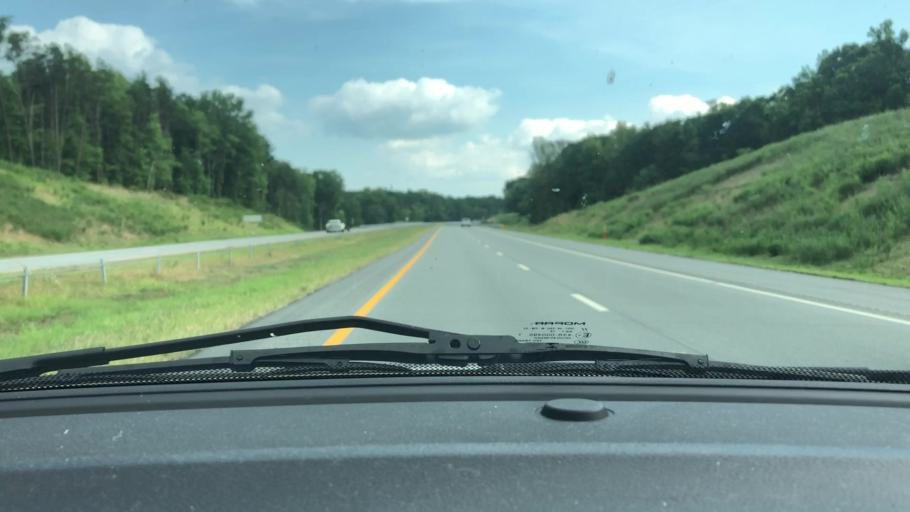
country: US
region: North Carolina
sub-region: Guilford County
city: Oak Ridge
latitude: 36.1502
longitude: -79.9592
